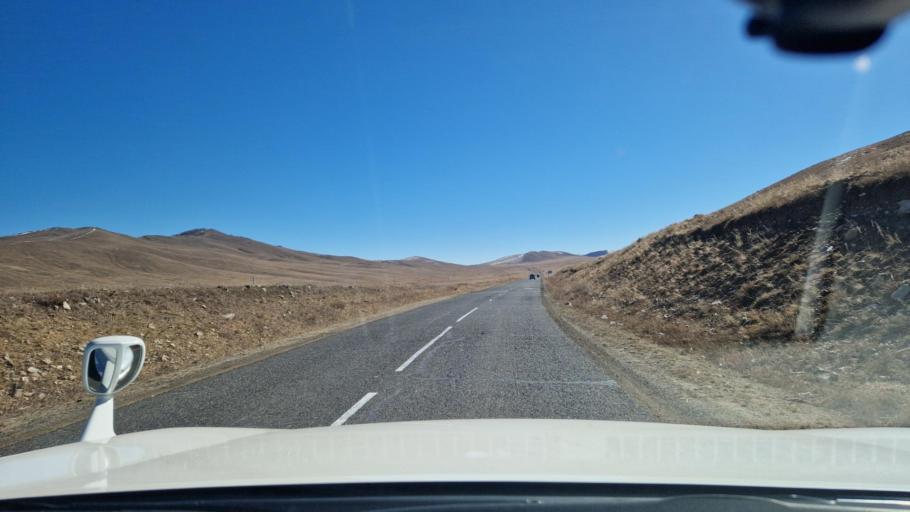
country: MN
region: Hentiy
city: Modot
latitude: 47.8057
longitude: 108.8130
